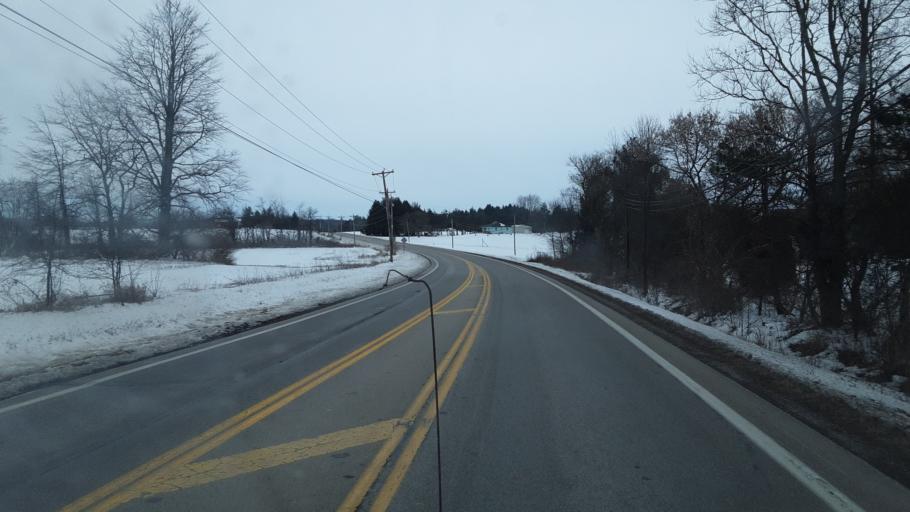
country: US
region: Ohio
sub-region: Union County
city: New California
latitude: 40.1485
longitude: -83.2443
